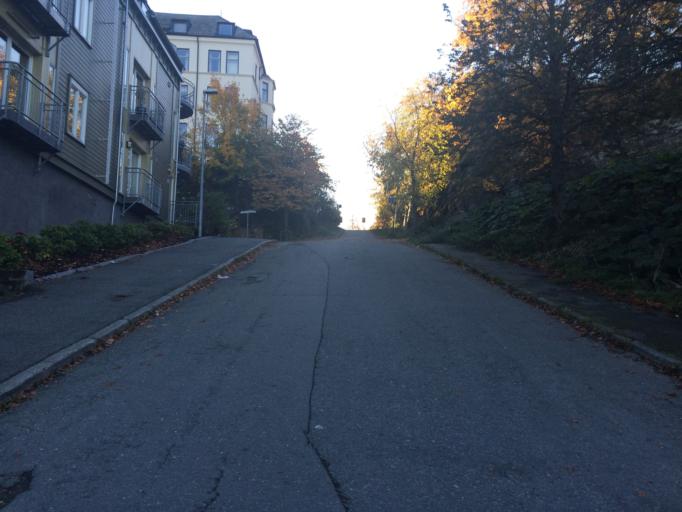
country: NO
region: Sor-Trondelag
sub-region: Trondheim
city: Trondheim
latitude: 63.4326
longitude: 10.4151
